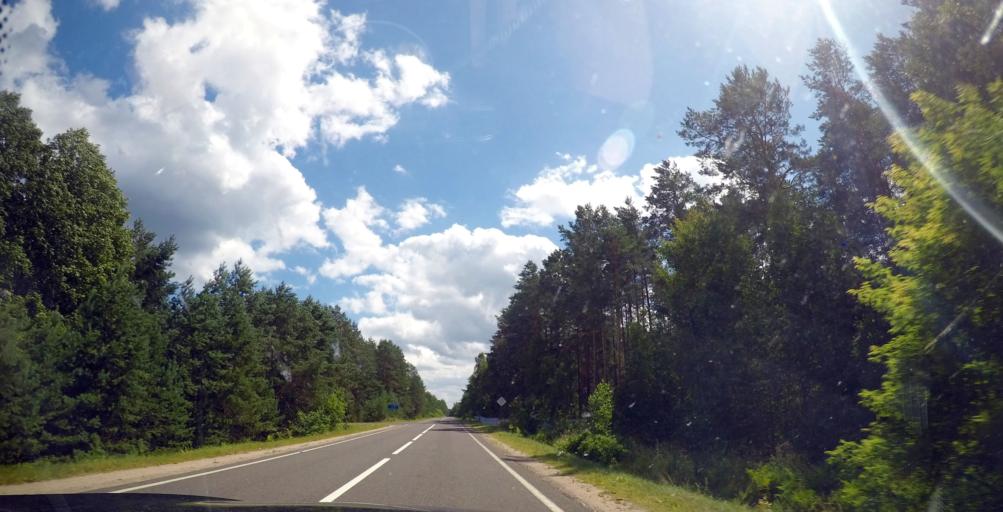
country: LT
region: Alytaus apskritis
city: Druskininkai
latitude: 53.8771
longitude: 24.1468
